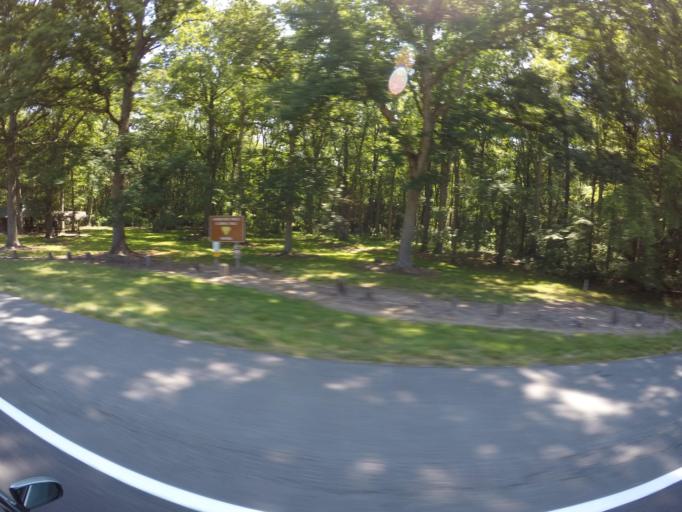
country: US
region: Delaware
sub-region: Sussex County
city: Georgetown
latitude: 38.7883
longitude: -75.4383
